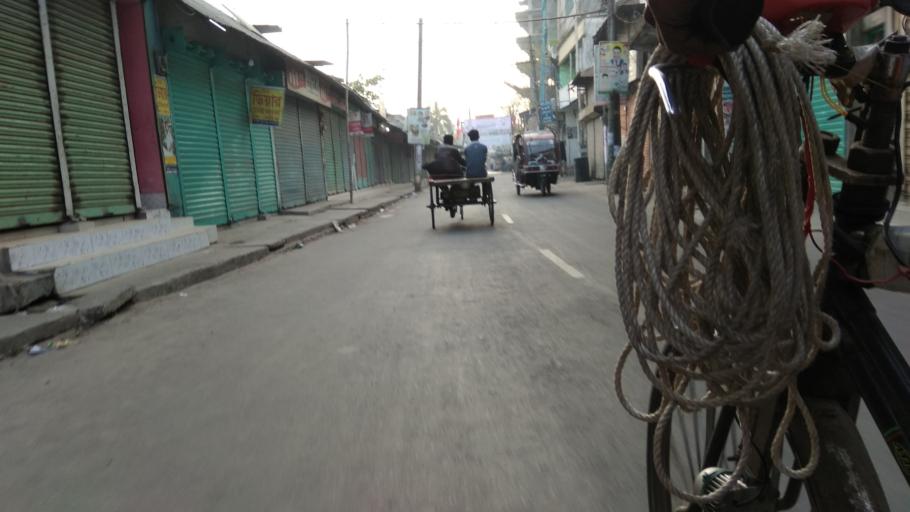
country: BD
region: Barisal
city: Mehendiganj
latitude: 22.9145
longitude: 90.4115
